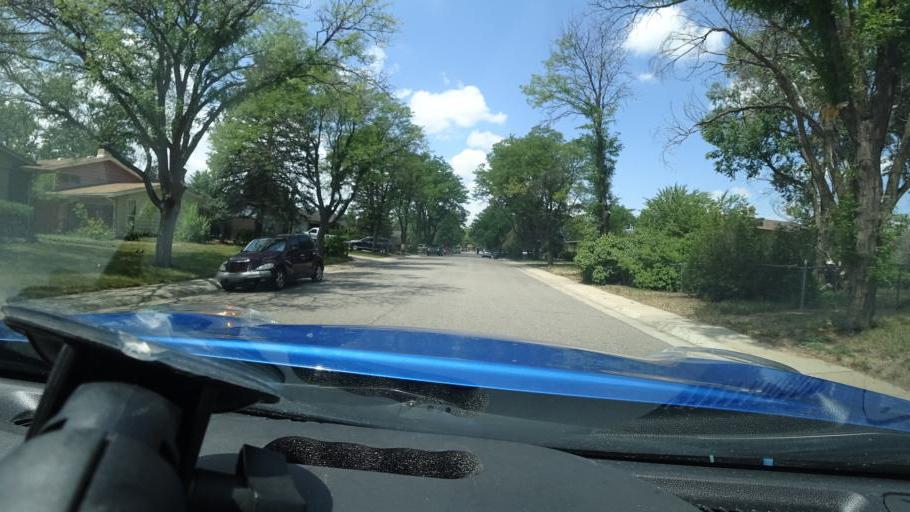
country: US
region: Colorado
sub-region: Adams County
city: Aurora
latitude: 39.7034
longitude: -104.8402
